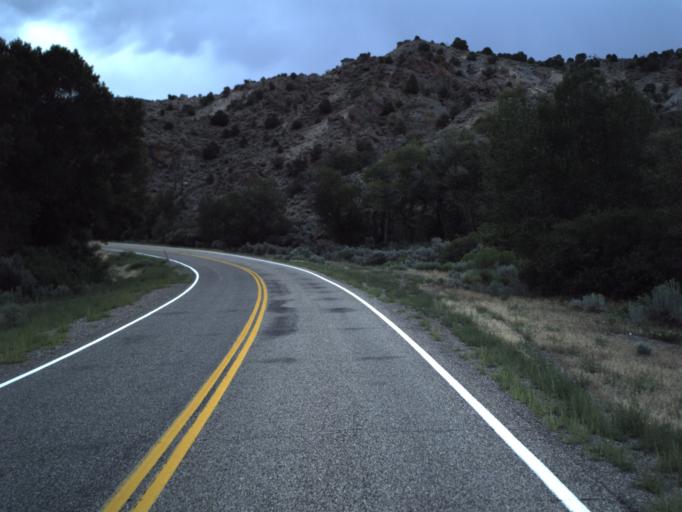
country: US
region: Utah
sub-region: Piute County
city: Junction
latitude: 38.2007
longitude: -112.1680
